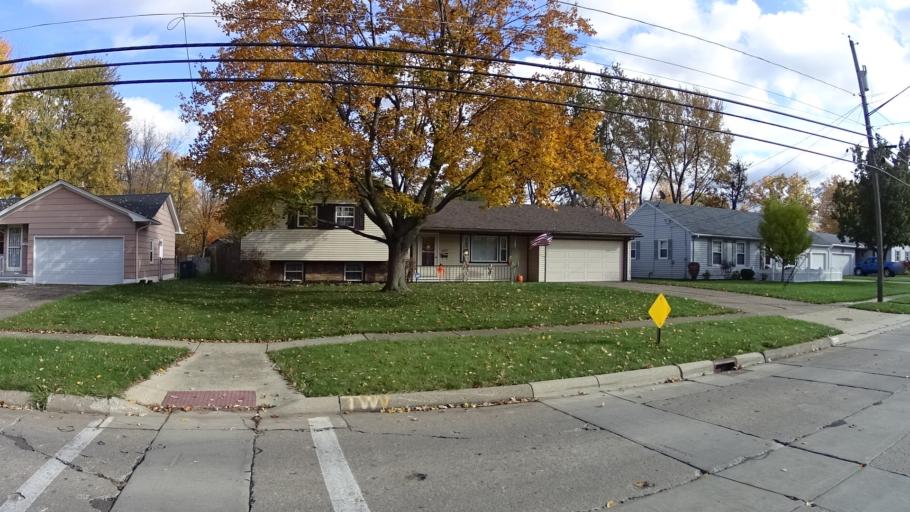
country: US
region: Ohio
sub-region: Lorain County
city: Lorain
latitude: 41.4314
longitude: -82.1897
